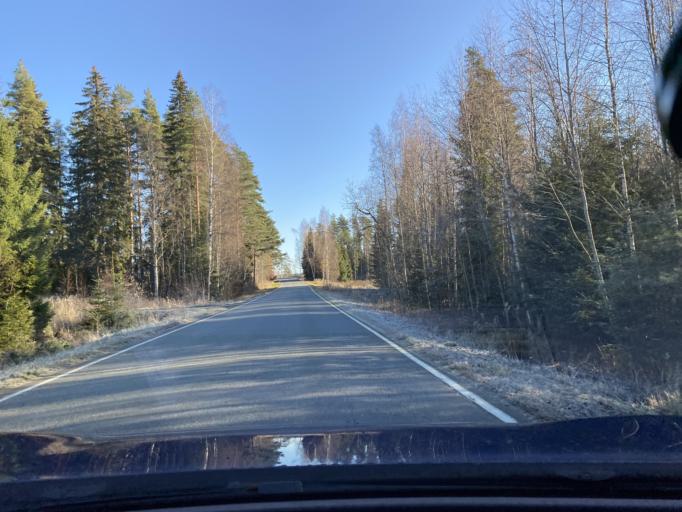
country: FI
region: Pirkanmaa
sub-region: Etelae-Pirkanmaa
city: Akaa
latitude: 61.0108
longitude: 23.8982
